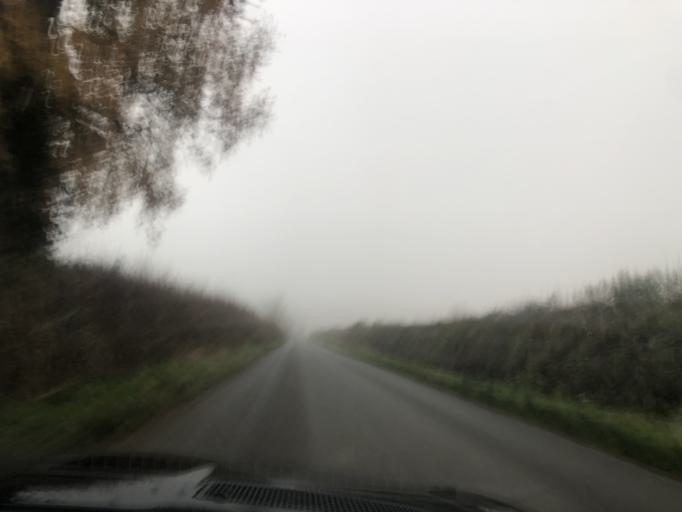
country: GB
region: England
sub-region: Oxfordshire
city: Bicester
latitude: 51.9173
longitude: -1.1777
